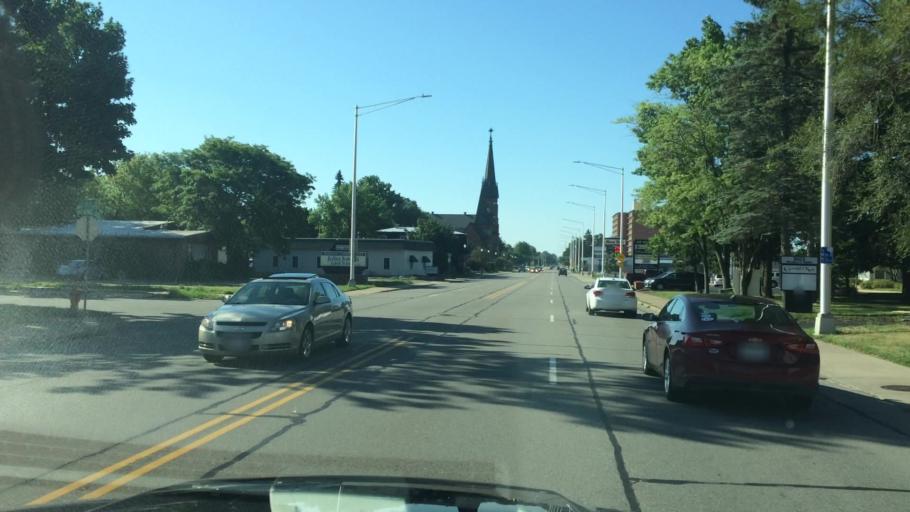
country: US
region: Wisconsin
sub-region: Marathon County
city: Wausau
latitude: 44.9560
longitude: -89.6244
